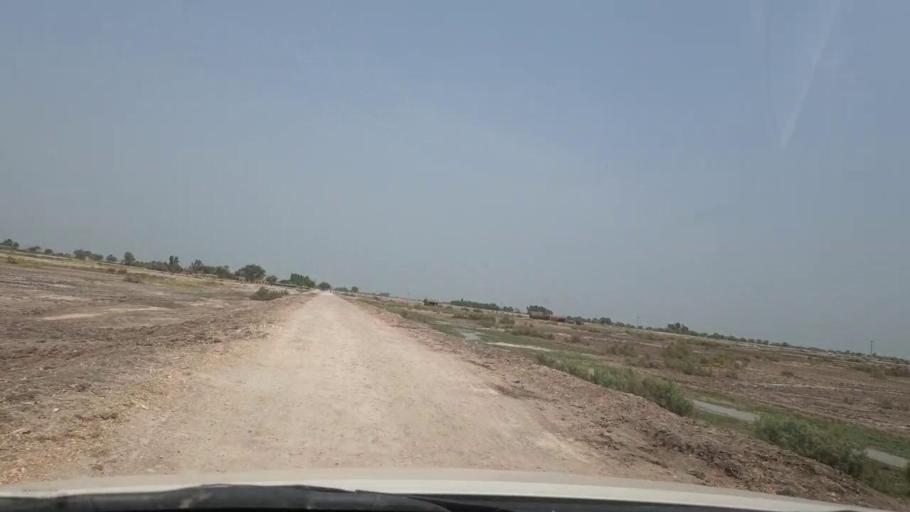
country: PK
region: Sindh
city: Rustam jo Goth
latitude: 28.0734
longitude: 68.8177
